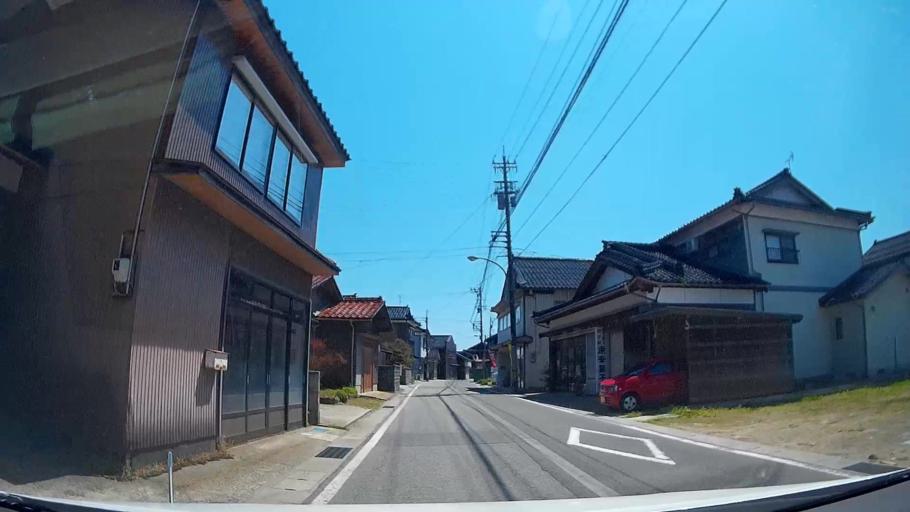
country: JP
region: Ishikawa
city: Nanao
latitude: 37.4053
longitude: 137.2419
